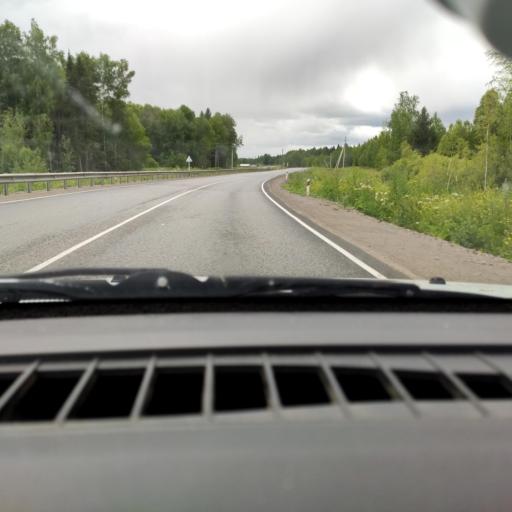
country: RU
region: Perm
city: Kungur
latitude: 57.3326
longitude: 56.9647
